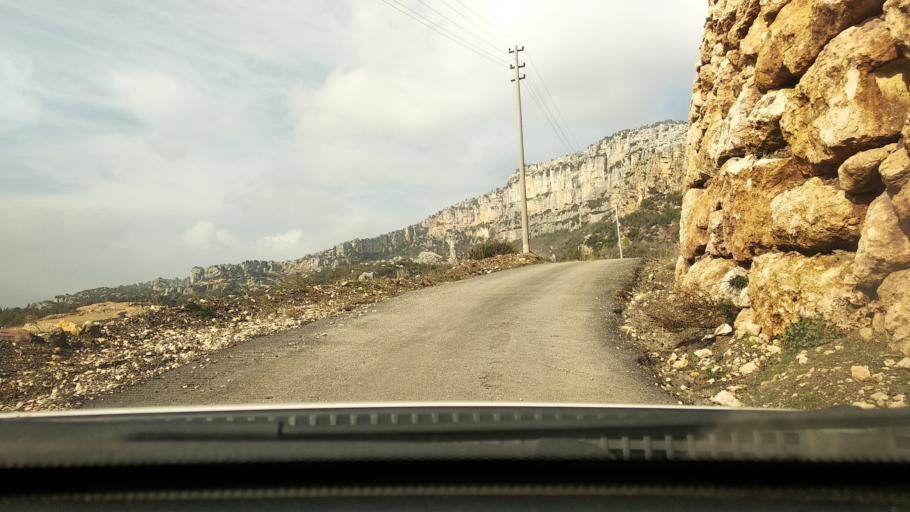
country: TR
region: Mersin
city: Kuzucubelen
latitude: 36.8755
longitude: 34.4727
